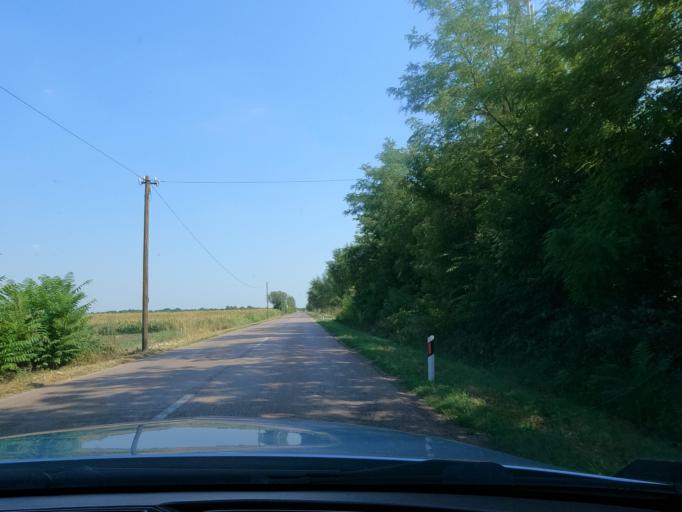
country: RS
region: Autonomna Pokrajina Vojvodina
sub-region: Severnobacki Okrug
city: Mali Igos
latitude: 45.7691
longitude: 19.7368
